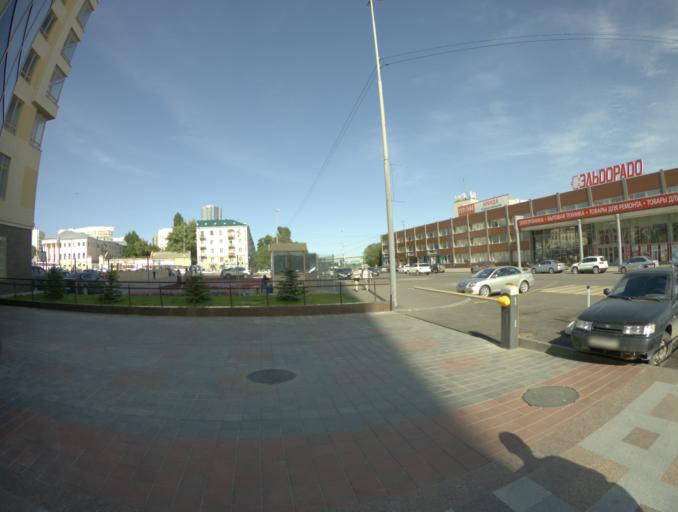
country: RU
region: Saratov
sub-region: Saratovskiy Rayon
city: Saratov
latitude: 51.5265
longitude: 46.0546
